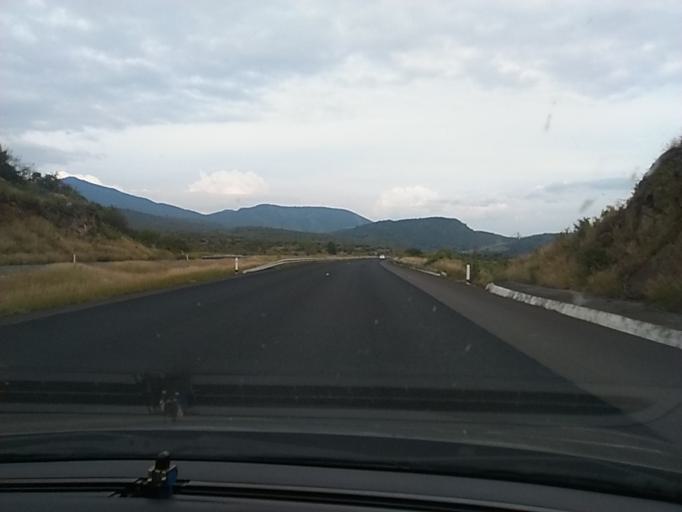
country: MX
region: Mexico
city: Huaniqueo de Morales
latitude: 19.8862
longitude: -101.4790
